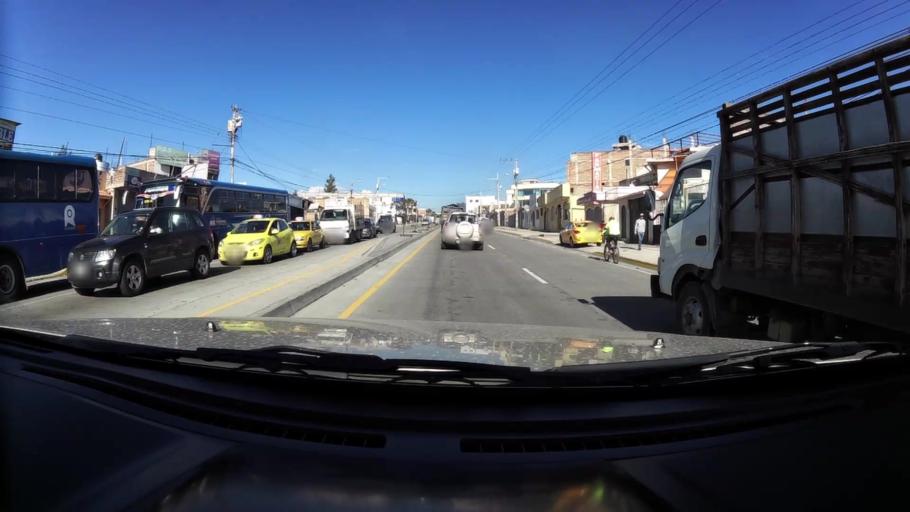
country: EC
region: Chimborazo
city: Riobamba
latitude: -1.6585
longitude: -78.6869
